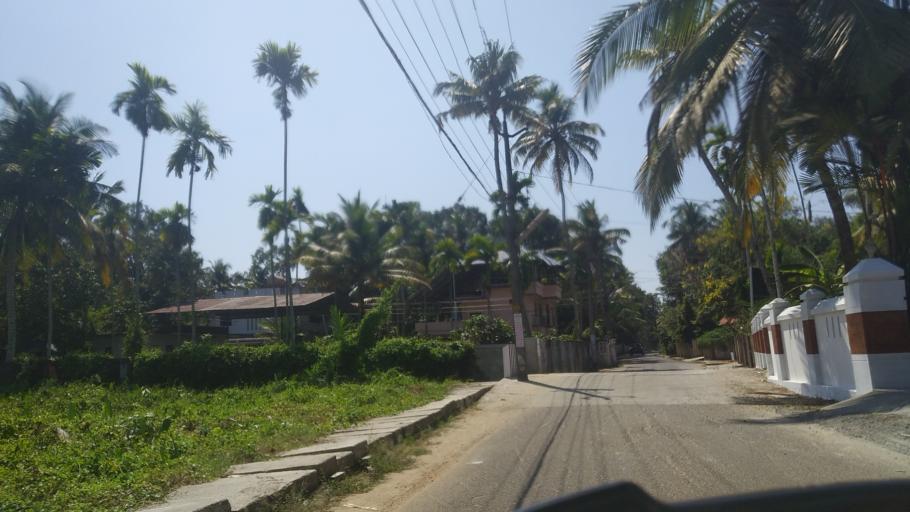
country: IN
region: Kerala
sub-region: Ernakulam
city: Elur
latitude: 10.1321
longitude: 76.2365
